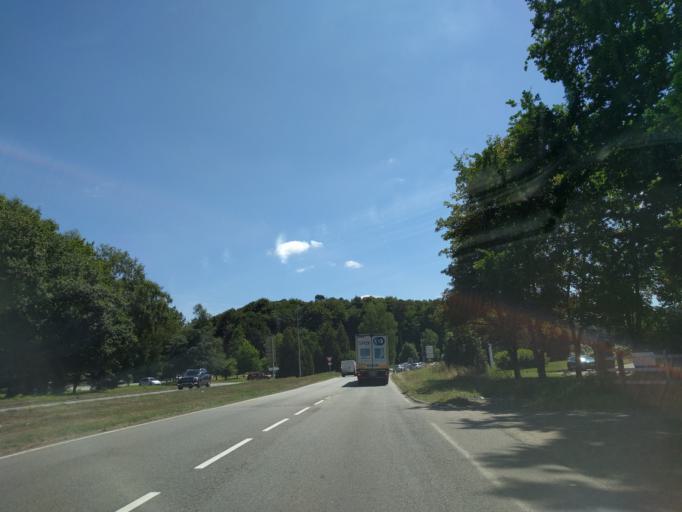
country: FR
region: Brittany
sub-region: Departement du Finistere
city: Quimper
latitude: 47.9795
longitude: -4.0964
